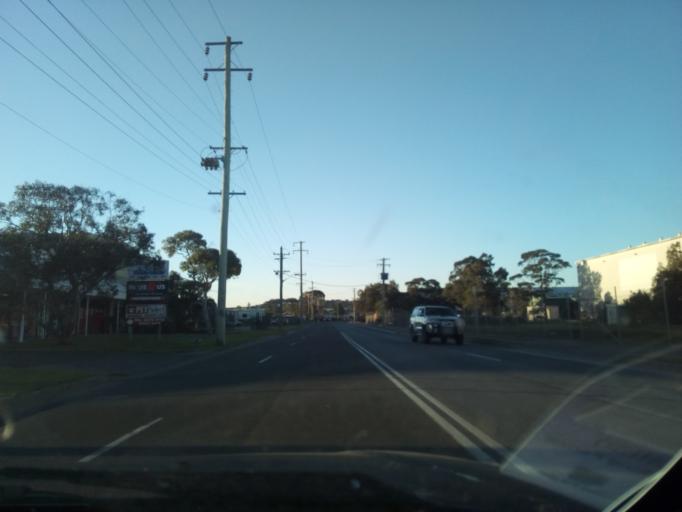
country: AU
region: New South Wales
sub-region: Wollongong
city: Port Kembla
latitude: -34.4966
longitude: 150.8917
